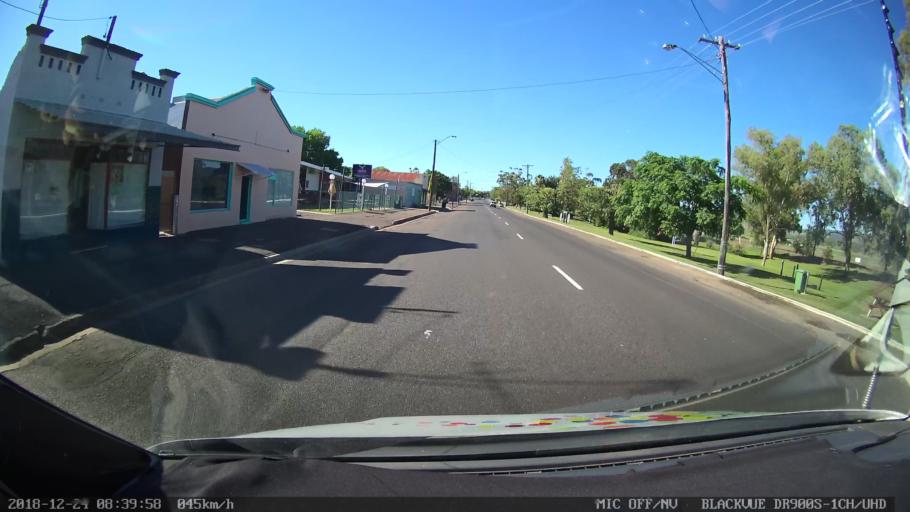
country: AU
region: New South Wales
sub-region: Liverpool Plains
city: Quirindi
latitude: -31.3516
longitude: 150.6470
